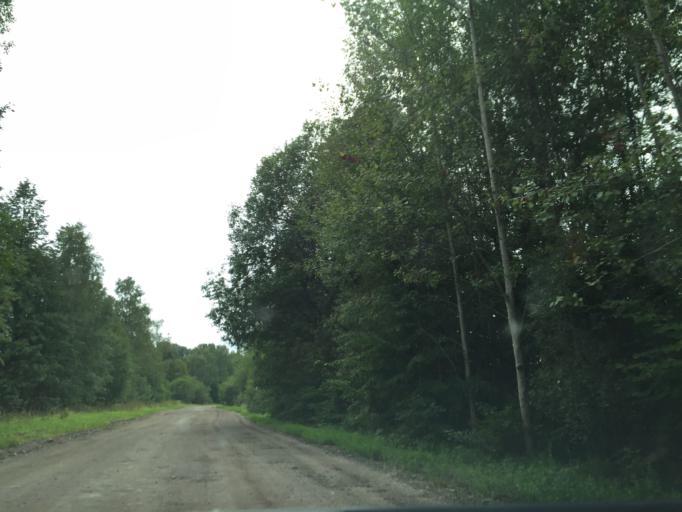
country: LV
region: Lielvarde
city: Lielvarde
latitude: 56.7547
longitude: 24.8407
